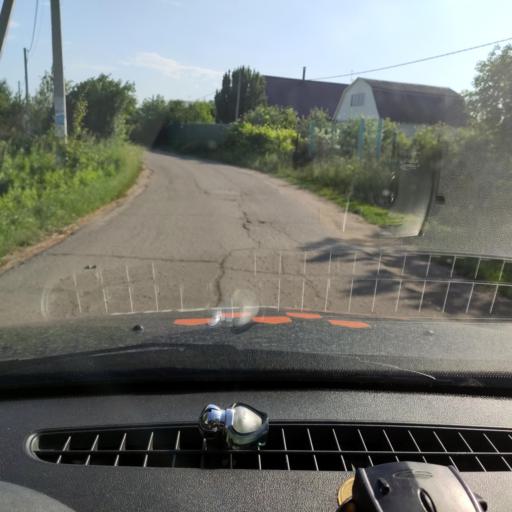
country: RU
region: Voronezj
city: Podkletnoye
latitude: 51.6198
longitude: 39.4470
